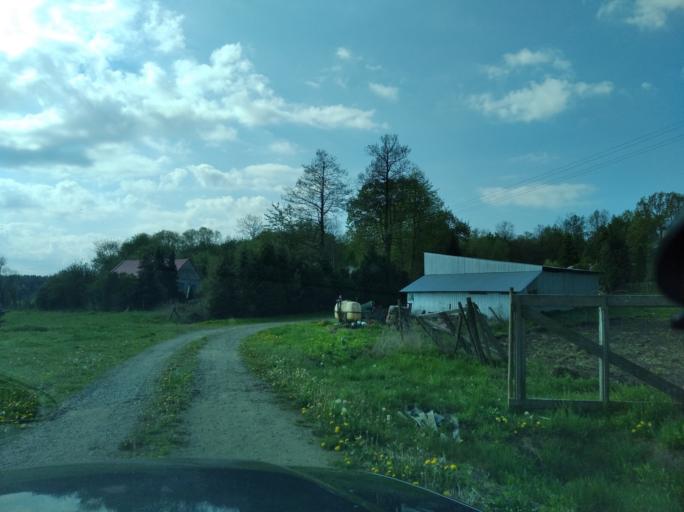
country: PL
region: Subcarpathian Voivodeship
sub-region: Powiat lubaczowski
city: Wielkie Oczy
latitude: 49.9736
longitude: 23.0634
